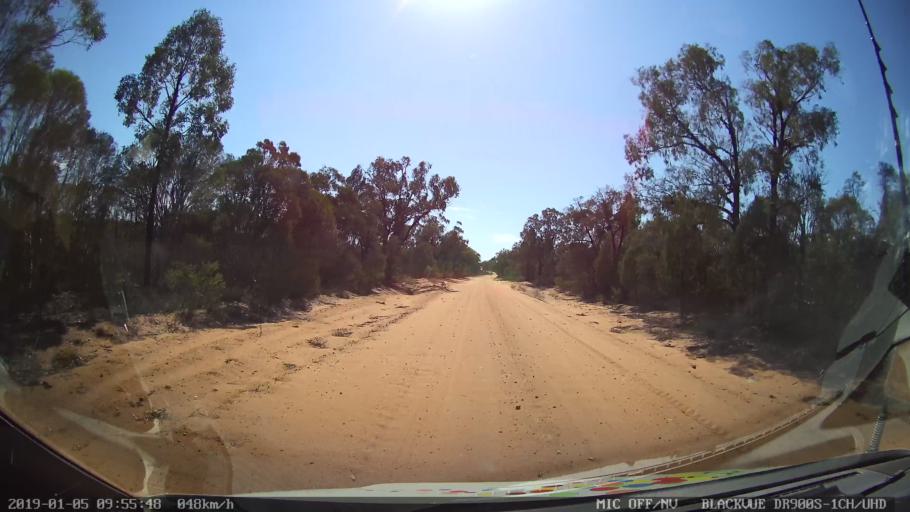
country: AU
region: New South Wales
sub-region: Gilgandra
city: Gilgandra
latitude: -31.6643
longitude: 148.7910
